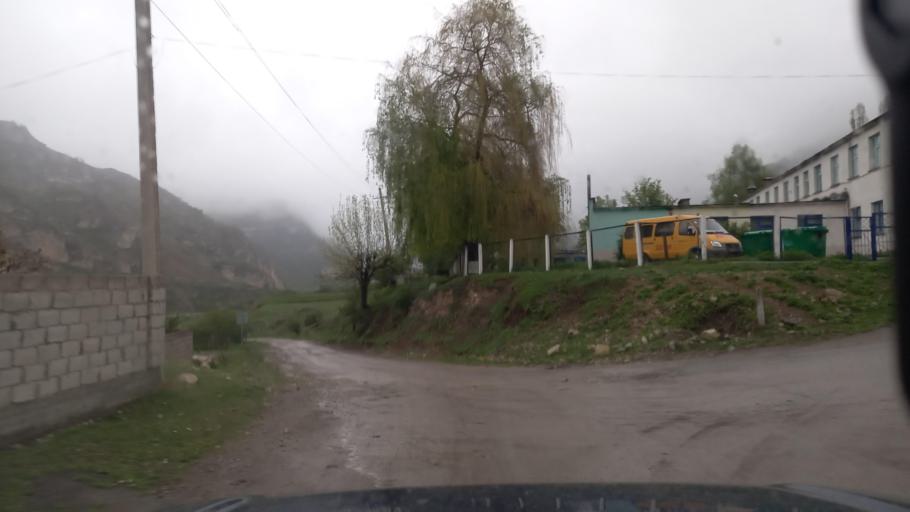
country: RU
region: Kabardino-Balkariya
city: Zhankhoteko
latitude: 43.5117
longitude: 43.1567
